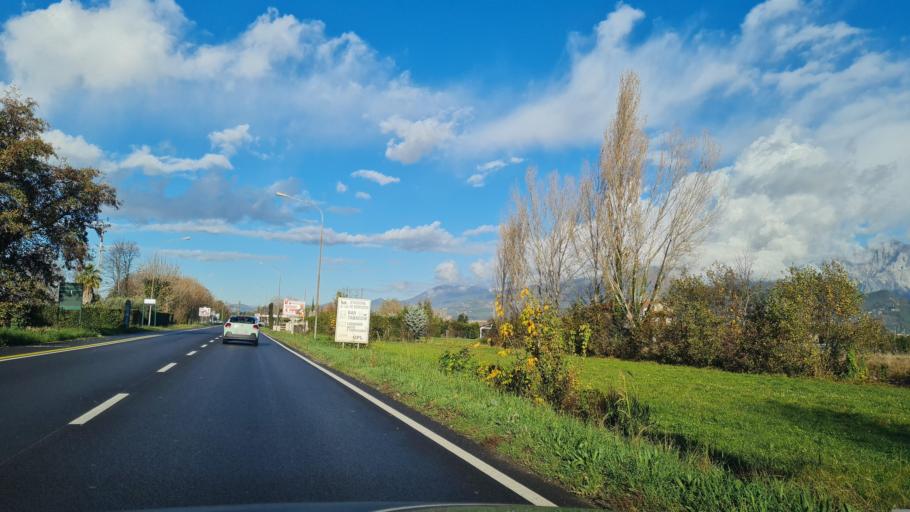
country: IT
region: Tuscany
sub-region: Provincia di Lucca
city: Pietrasanta
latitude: 43.9486
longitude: 10.2045
